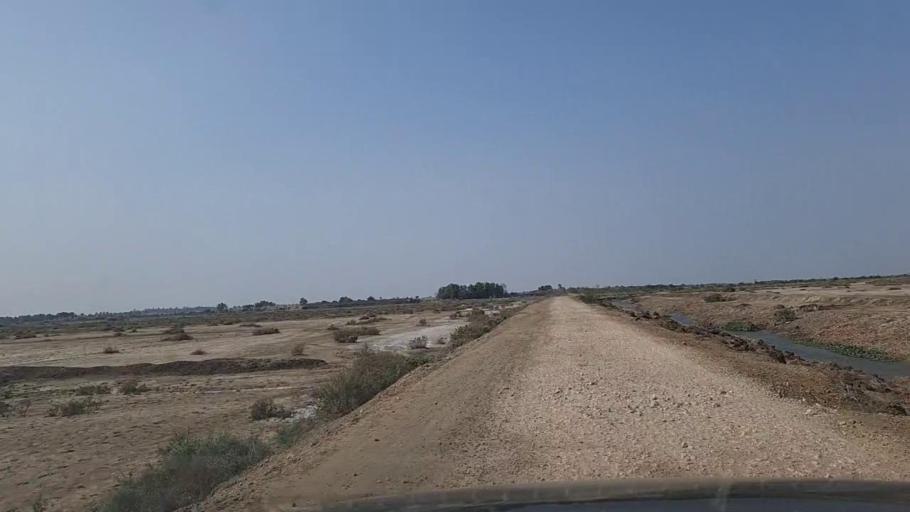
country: PK
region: Sindh
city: Gharo
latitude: 24.7019
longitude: 67.5878
